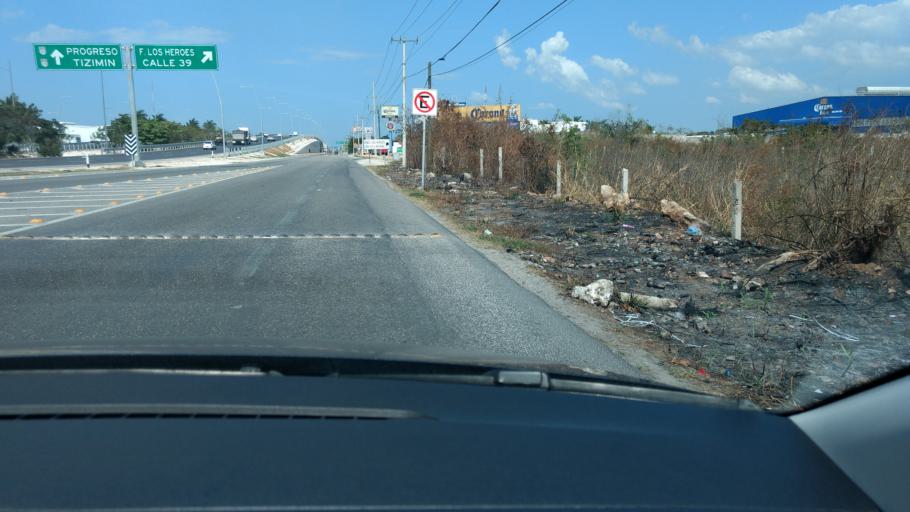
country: MX
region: Yucatan
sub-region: Kanasin
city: Kanasin
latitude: 20.9775
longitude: -89.5641
